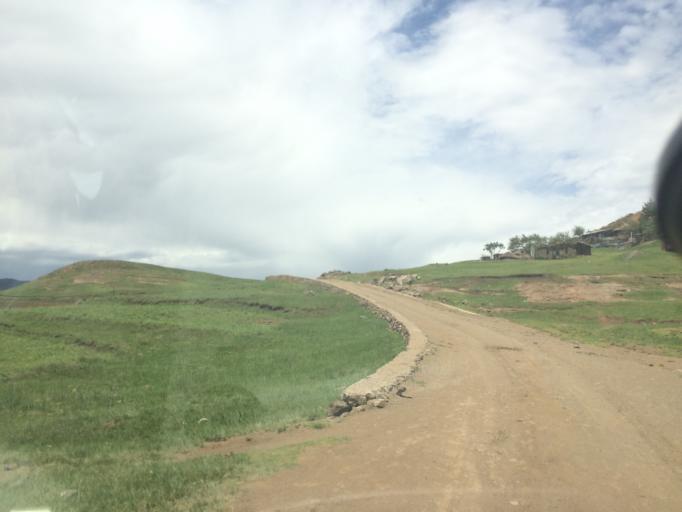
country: LS
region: Maseru
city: Nako
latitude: -29.8649
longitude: 28.0376
